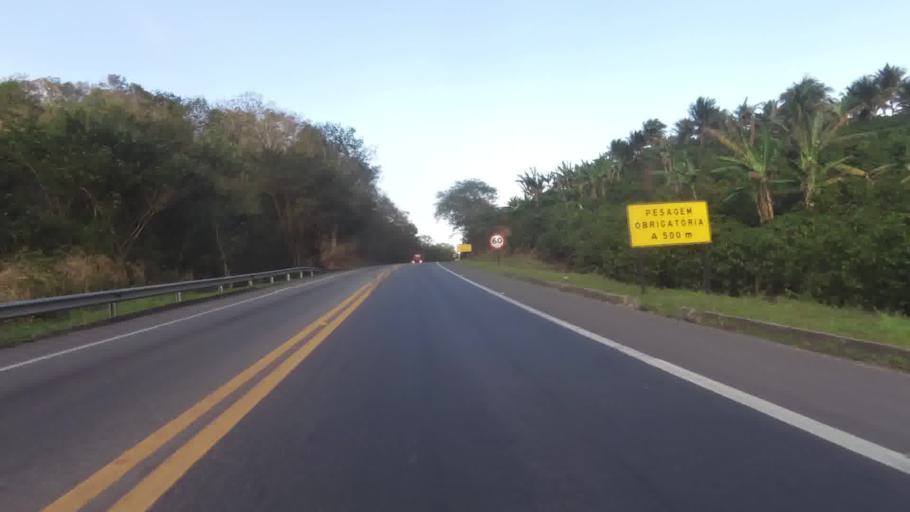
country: BR
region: Espirito Santo
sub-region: Rio Novo Do Sul
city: Rio Novo do Sul
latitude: -20.8653
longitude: -40.9204
